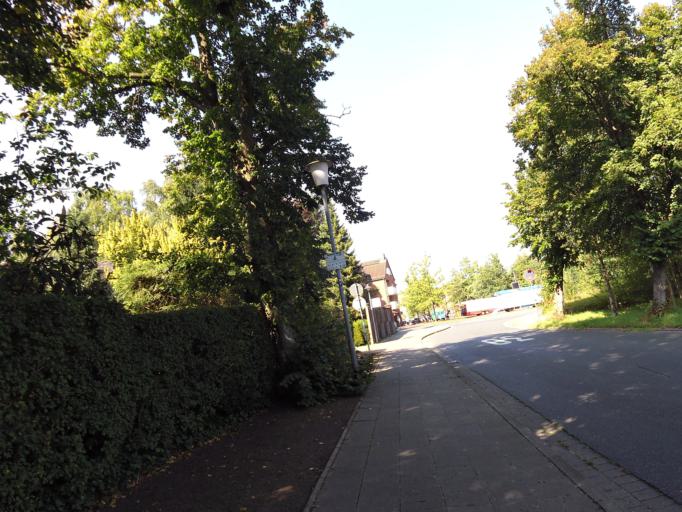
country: DE
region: Lower Saxony
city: Soltau
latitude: 52.9830
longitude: 9.8396
